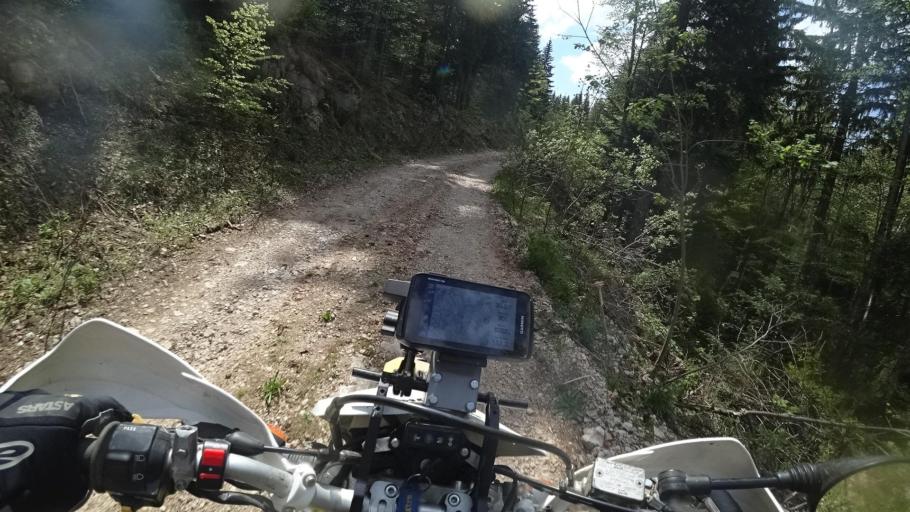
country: BA
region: Republika Srpska
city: Sipovo
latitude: 44.1533
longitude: 17.0334
